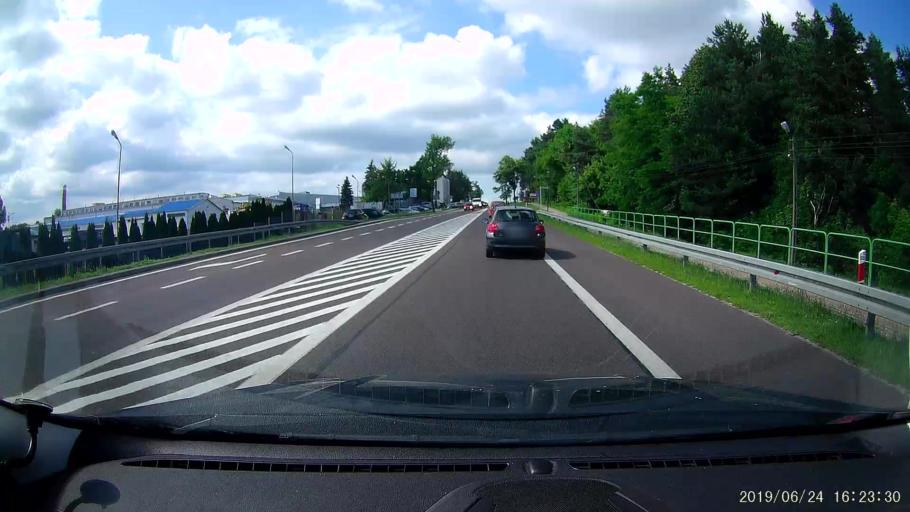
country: PL
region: Lublin Voivodeship
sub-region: Powiat tomaszowski
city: Tomaszow Lubelski
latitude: 50.4324
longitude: 23.4213
